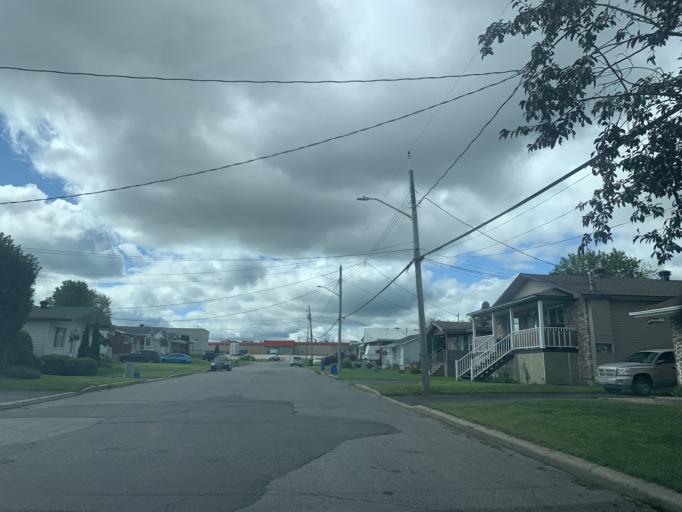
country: CA
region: Ontario
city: Hawkesbury
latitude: 45.6069
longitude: -74.5976
